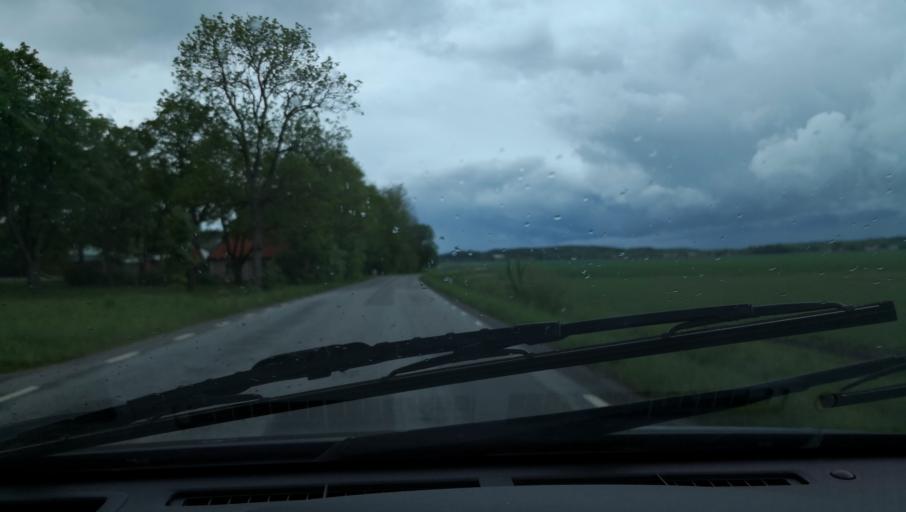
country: SE
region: Uppsala
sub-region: Enkopings Kommun
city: Orsundsbro
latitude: 59.7218
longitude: 17.3346
